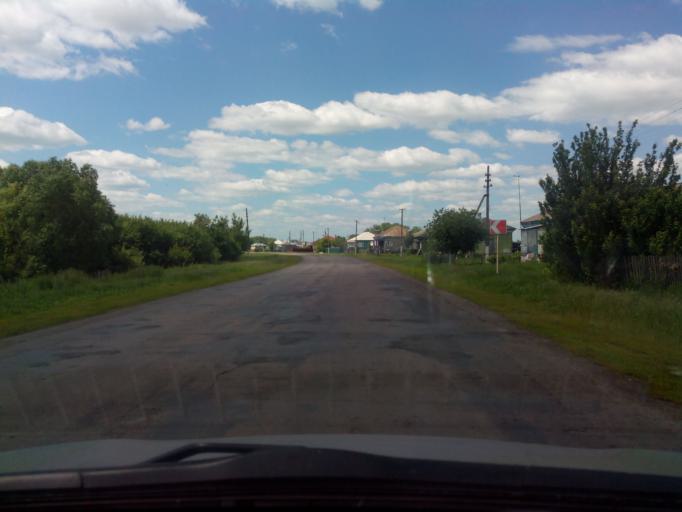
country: RU
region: Voronezj
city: Gribanovskiy
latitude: 51.6261
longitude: 41.9226
